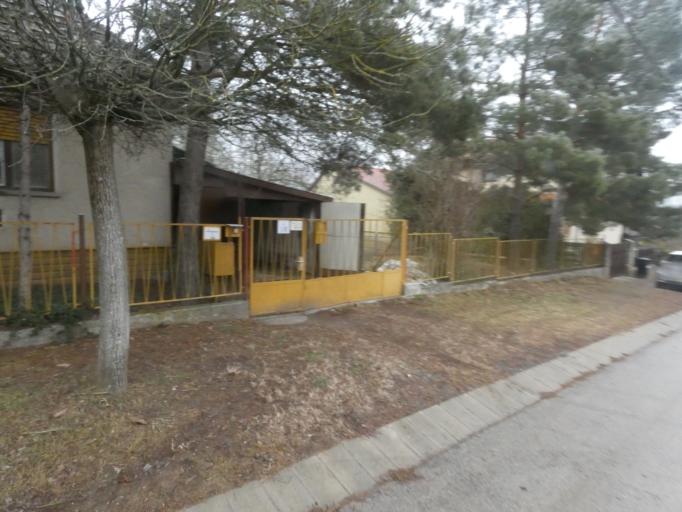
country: HU
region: Pest
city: Veresegyhaz
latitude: 47.6498
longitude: 19.2781
